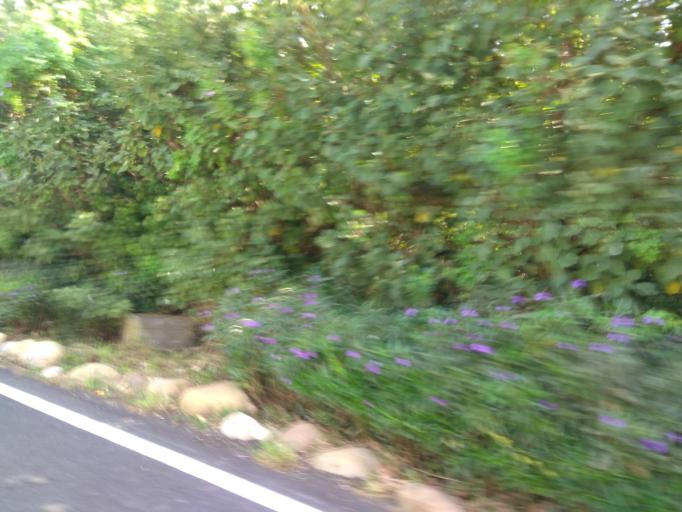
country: TW
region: Taiwan
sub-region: Hsinchu
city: Zhubei
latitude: 24.9926
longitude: 121.0187
